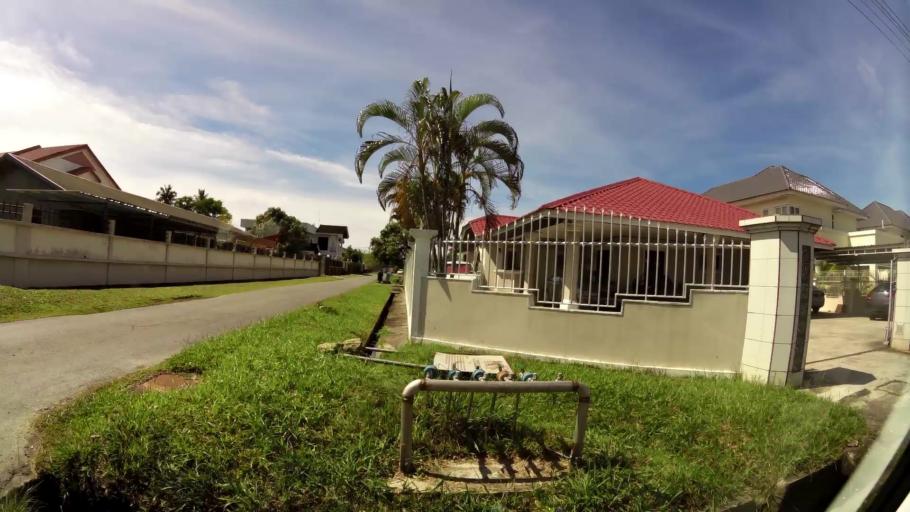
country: BN
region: Belait
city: Kuala Belait
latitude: 4.5870
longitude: 114.2132
